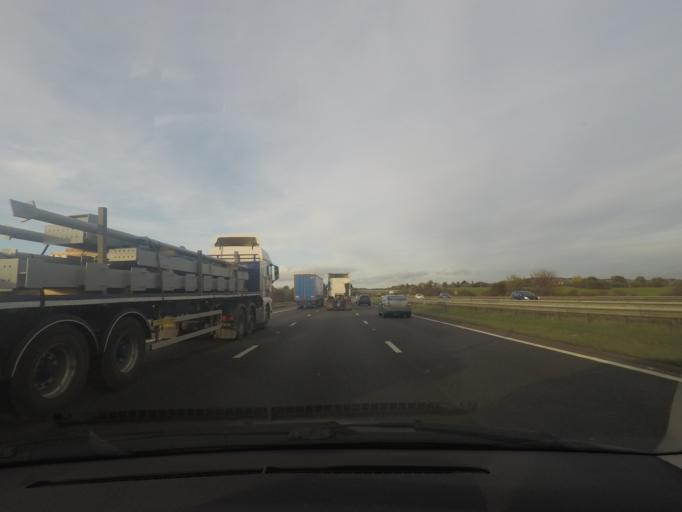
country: GB
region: England
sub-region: Barnsley
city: Darton
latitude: 53.5768
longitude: -1.5397
